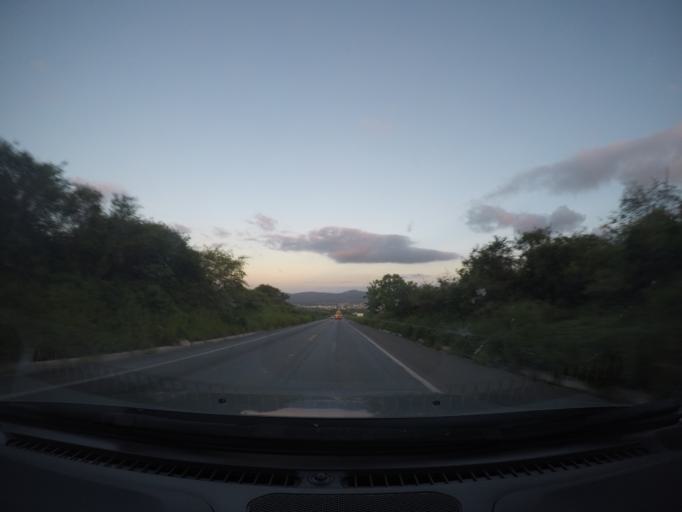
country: BR
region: Bahia
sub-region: Seabra
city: Seabra
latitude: -12.4324
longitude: -41.8078
